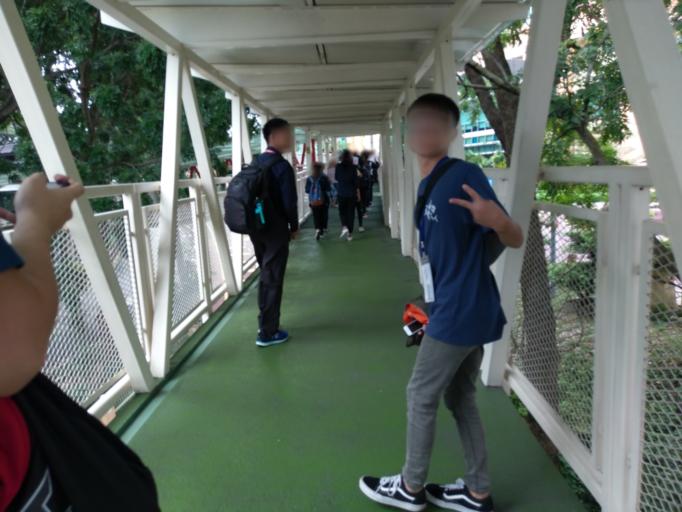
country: MY
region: Selangor
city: Subang Jaya
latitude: 3.0678
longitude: 101.6048
